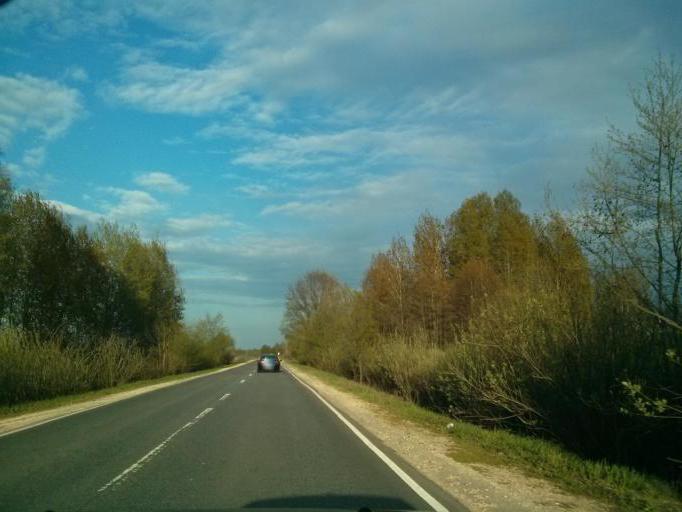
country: RU
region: Nizjnij Novgorod
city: Navashino
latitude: 55.6044
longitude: 42.1816
